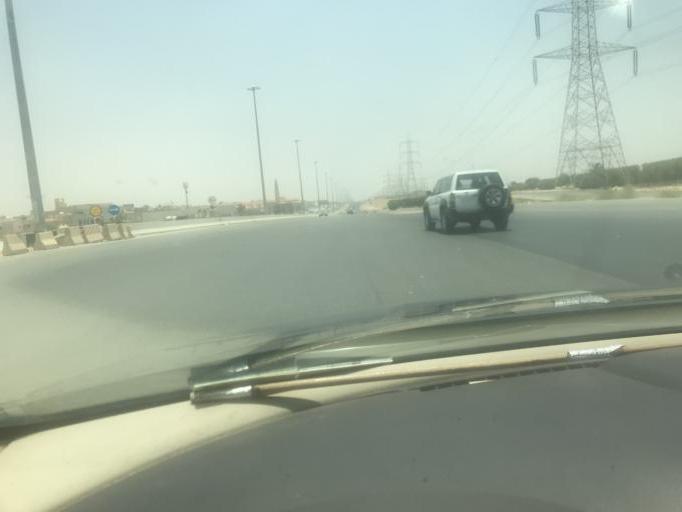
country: SA
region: Ar Riyad
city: Riyadh
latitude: 24.8122
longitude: 46.7220
